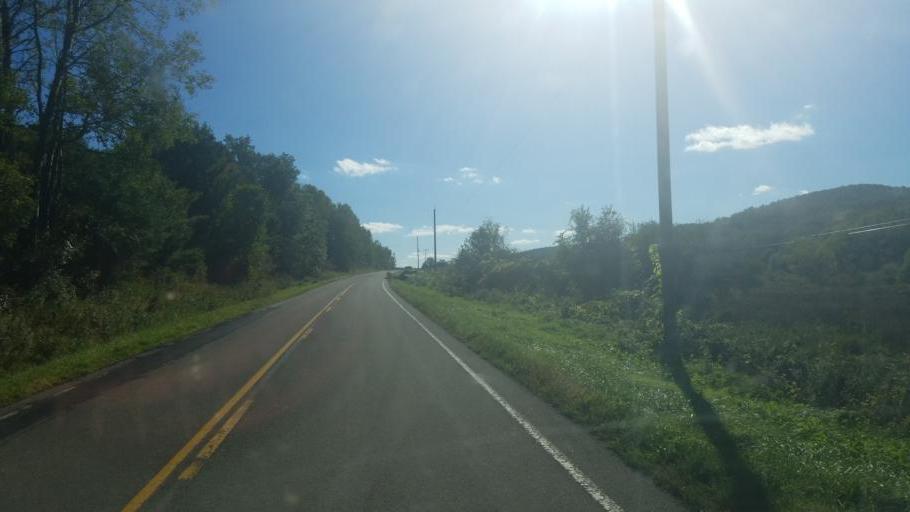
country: US
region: New York
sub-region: Allegany County
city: Friendship
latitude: 42.2882
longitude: -78.1201
